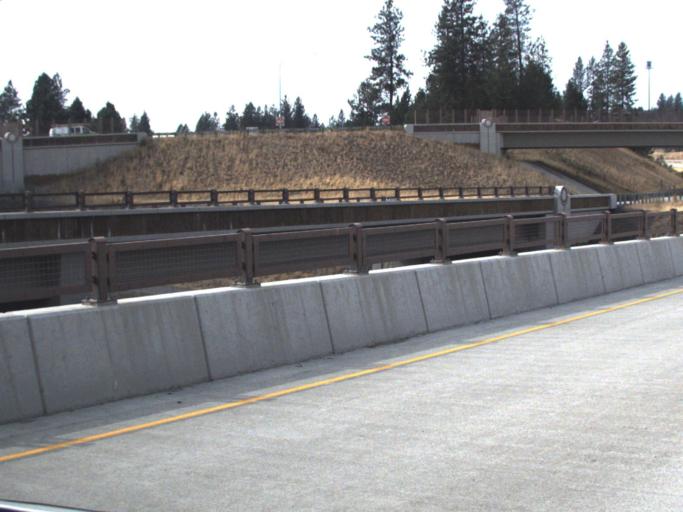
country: US
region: Washington
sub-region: Spokane County
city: Mead
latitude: 47.7755
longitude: -117.3729
